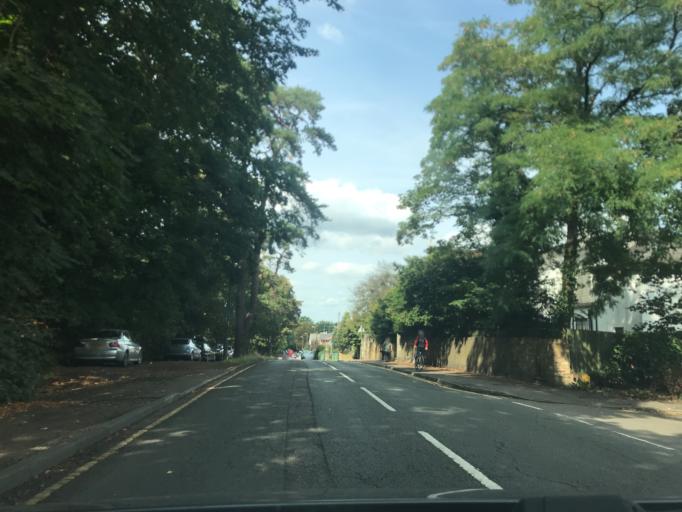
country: GB
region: England
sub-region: Surrey
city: Weybridge
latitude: 51.3656
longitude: -0.4600
